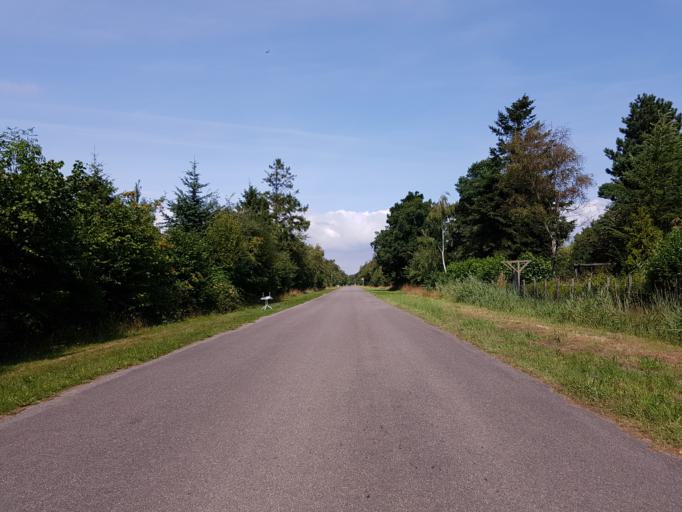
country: DK
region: Zealand
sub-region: Guldborgsund Kommune
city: Nykobing Falster
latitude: 54.5915
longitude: 11.9655
